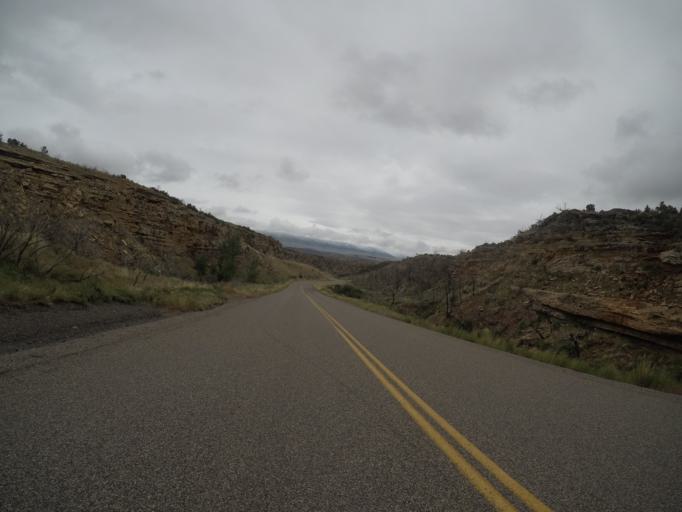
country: US
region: Wyoming
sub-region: Big Horn County
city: Lovell
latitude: 45.1088
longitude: -108.2383
